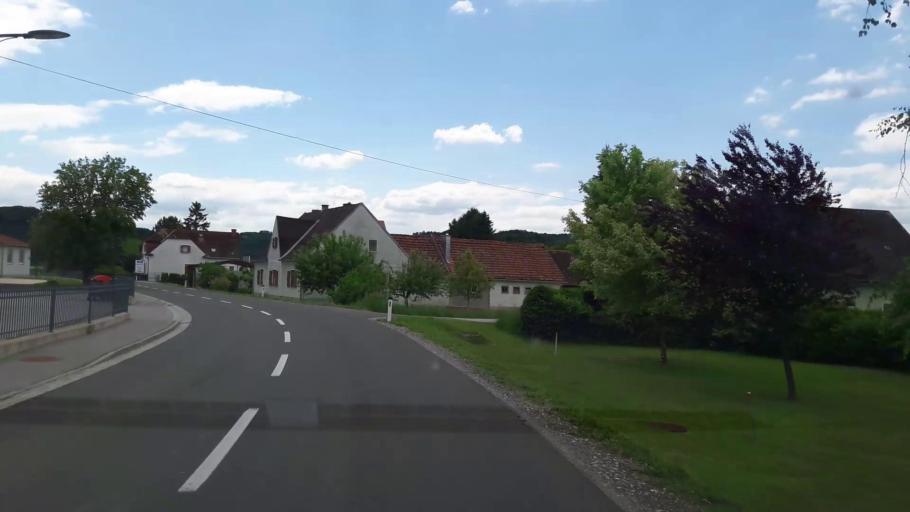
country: AT
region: Styria
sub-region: Politischer Bezirk Hartberg-Fuerstenfeld
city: UEbersbach
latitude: 47.0230
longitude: 16.0490
